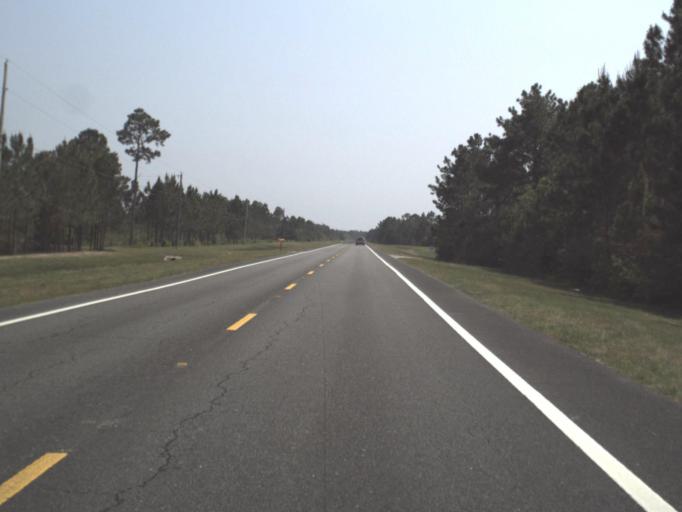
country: US
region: Florida
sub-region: Santa Rosa County
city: Bagdad
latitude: 30.4929
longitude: -87.0803
